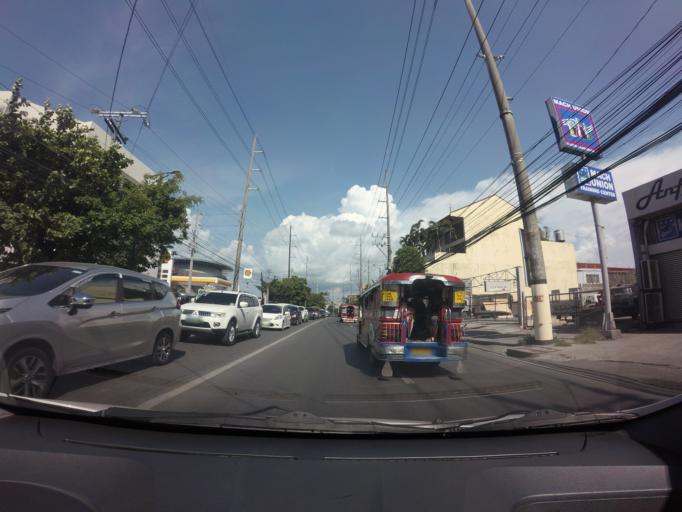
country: PH
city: Sambayanihan People's Village
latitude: 14.4426
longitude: 120.9969
